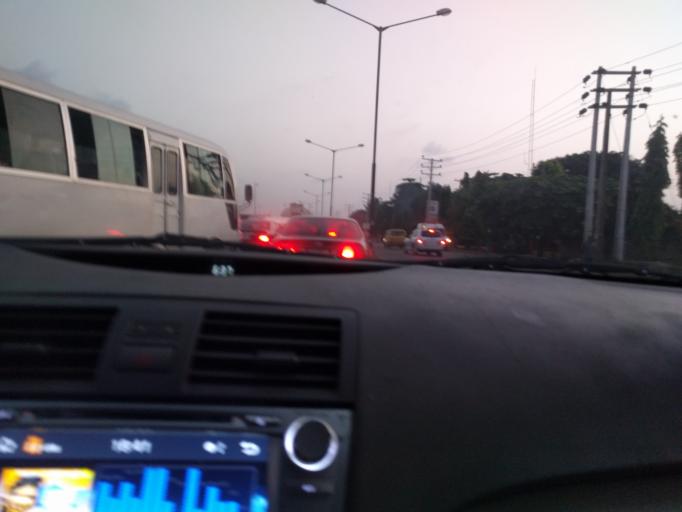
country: NG
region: Lagos
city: Oshodi
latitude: 6.5466
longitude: 3.3374
